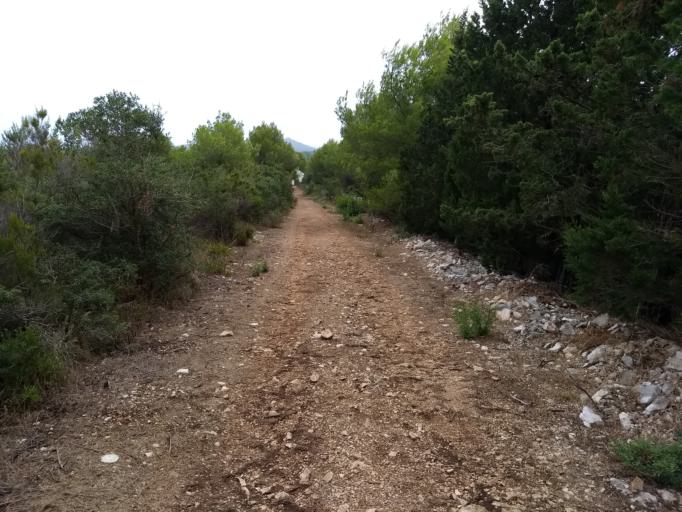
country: HR
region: Zadarska
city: Ugljan
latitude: 44.1441
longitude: 15.0783
